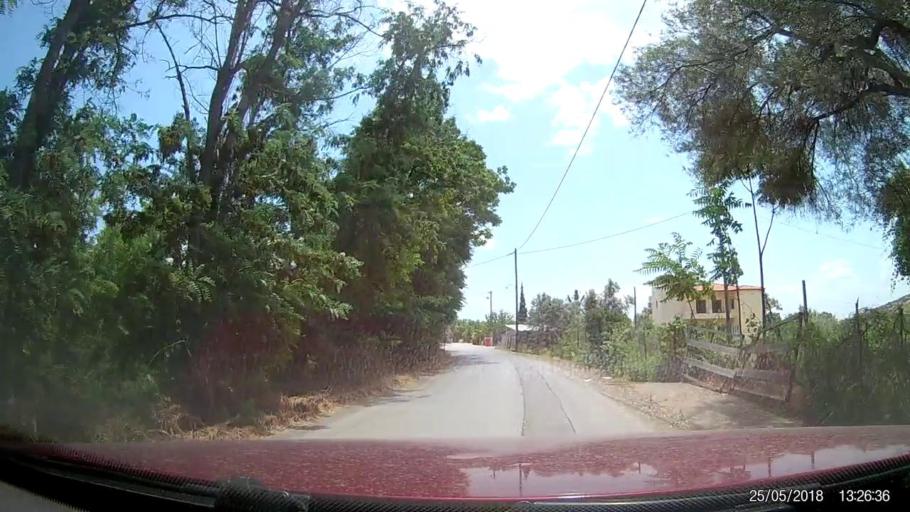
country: GR
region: Central Greece
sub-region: Nomos Evvoias
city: Mytikas
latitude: 38.4553
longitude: 23.6481
